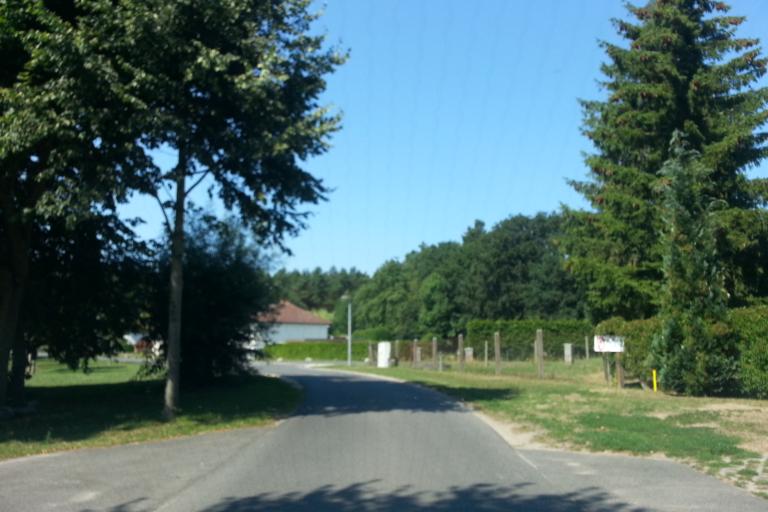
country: DE
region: Mecklenburg-Vorpommern
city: Ferdinandshof
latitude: 53.7053
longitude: 13.8340
